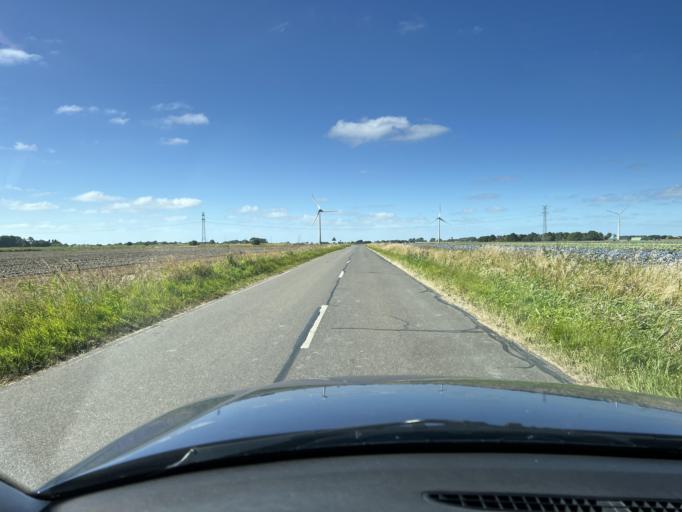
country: DE
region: Schleswig-Holstein
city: Norddeich
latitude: 54.2216
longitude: 8.9021
